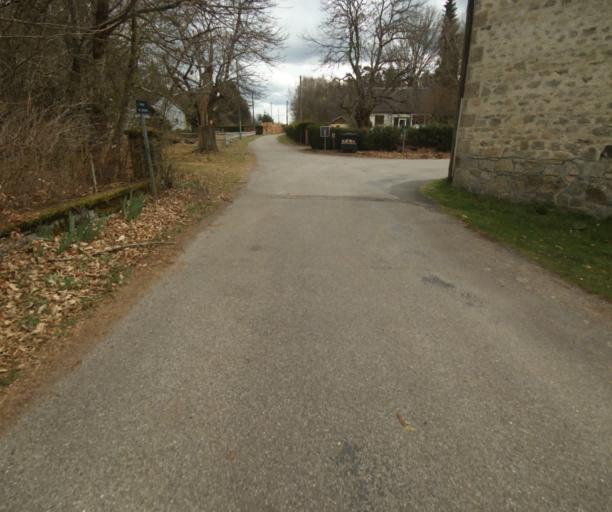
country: FR
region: Limousin
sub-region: Departement de la Correze
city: Correze
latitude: 45.2741
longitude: 1.9808
